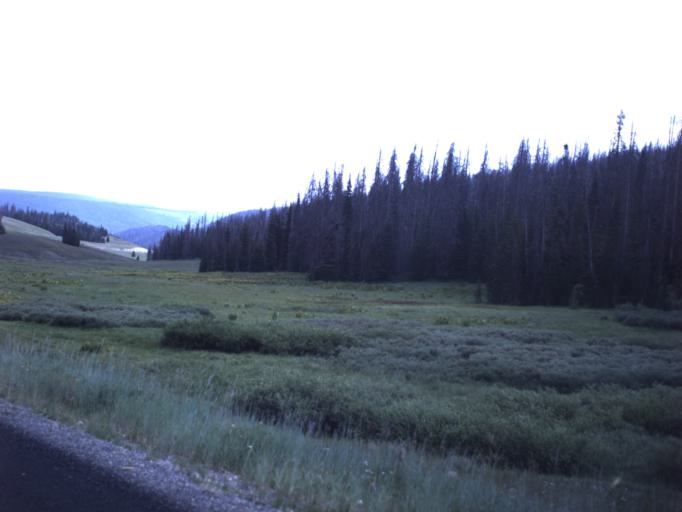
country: US
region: Utah
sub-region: Summit County
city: Francis
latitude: 40.4825
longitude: -111.0294
